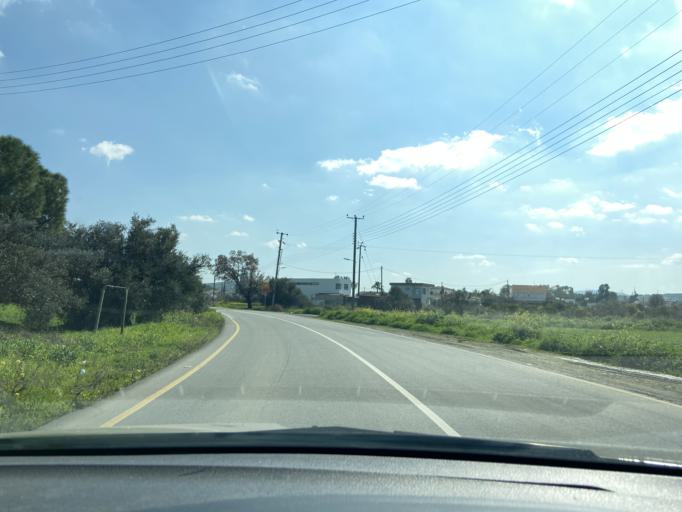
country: CY
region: Lefkosia
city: Dali
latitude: 35.0229
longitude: 33.3859
